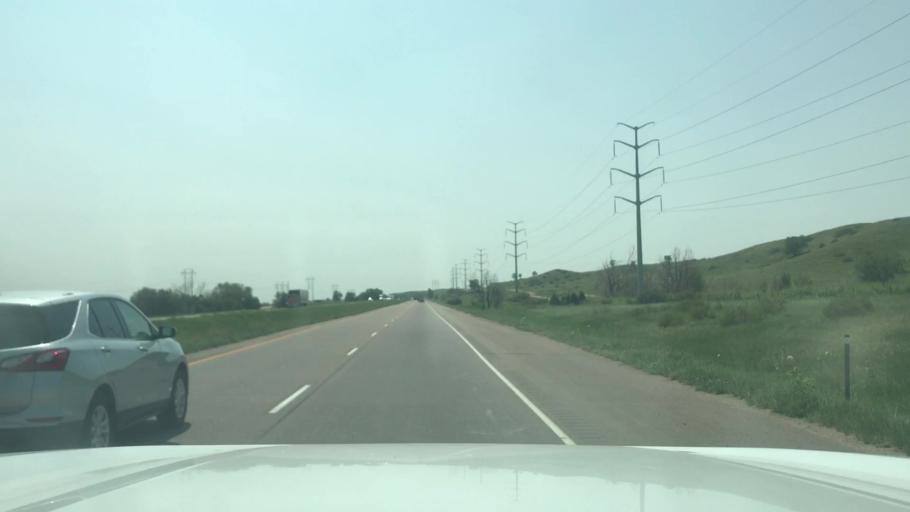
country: US
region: Colorado
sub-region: El Paso County
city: Fountain
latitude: 38.7035
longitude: -104.7229
